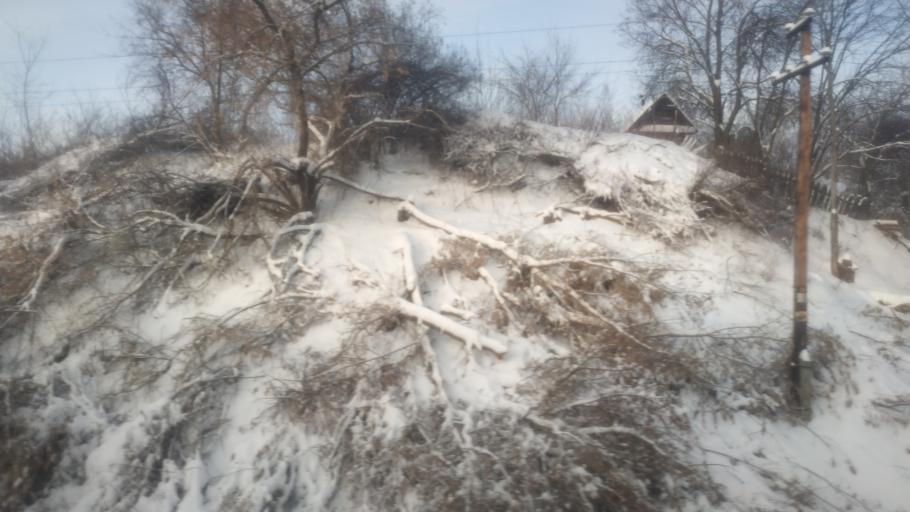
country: RU
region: Kirov
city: Sosnovka
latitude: 56.2519
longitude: 51.2263
